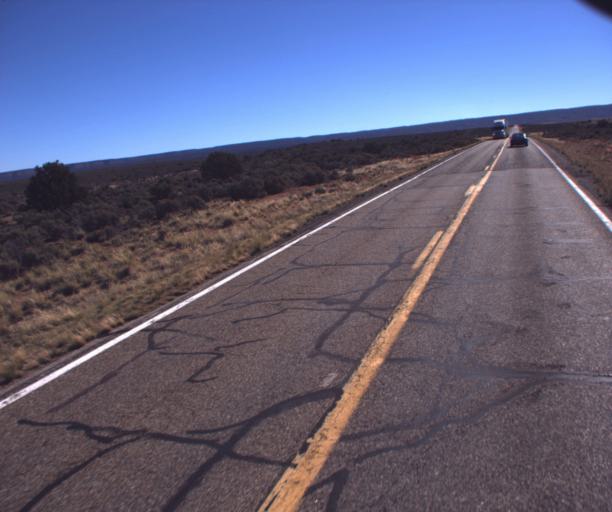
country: US
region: Arizona
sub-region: Coconino County
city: Fredonia
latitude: 36.8856
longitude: -112.3462
